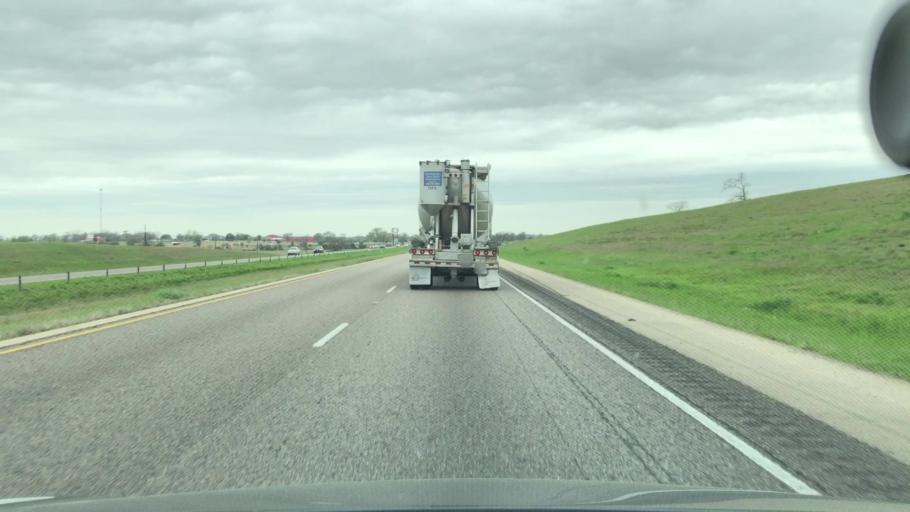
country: US
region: Texas
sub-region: Madison County
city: Madisonville
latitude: 31.0378
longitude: -95.9401
